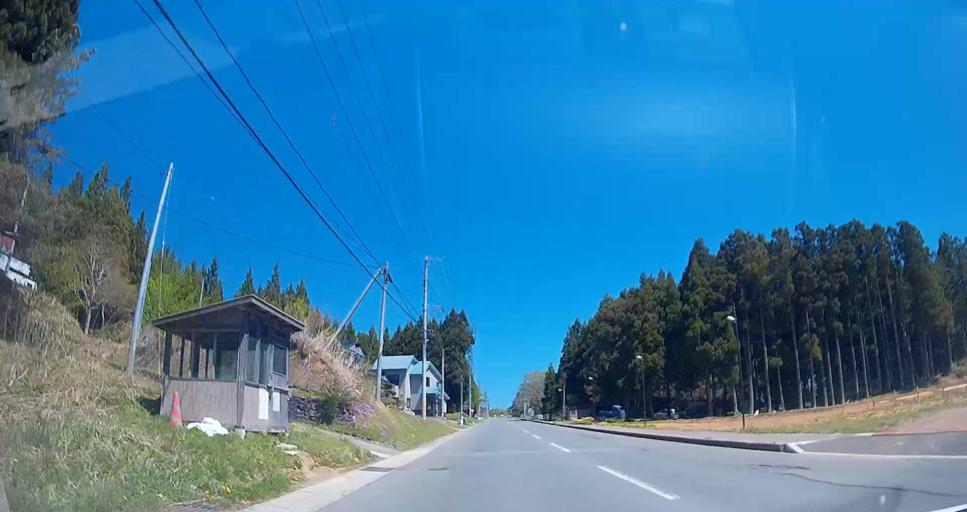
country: JP
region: Aomori
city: Mutsu
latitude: 41.0908
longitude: 141.3885
